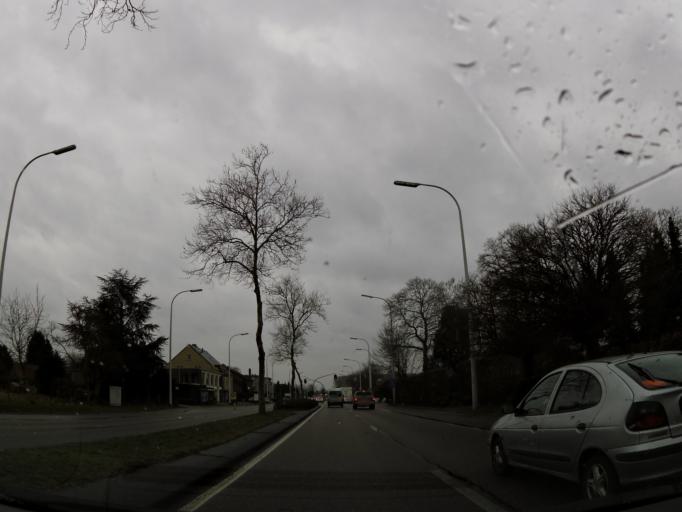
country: BE
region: Flanders
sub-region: Provincie Limburg
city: Maasmechelen
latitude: 50.9592
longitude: 5.6947
